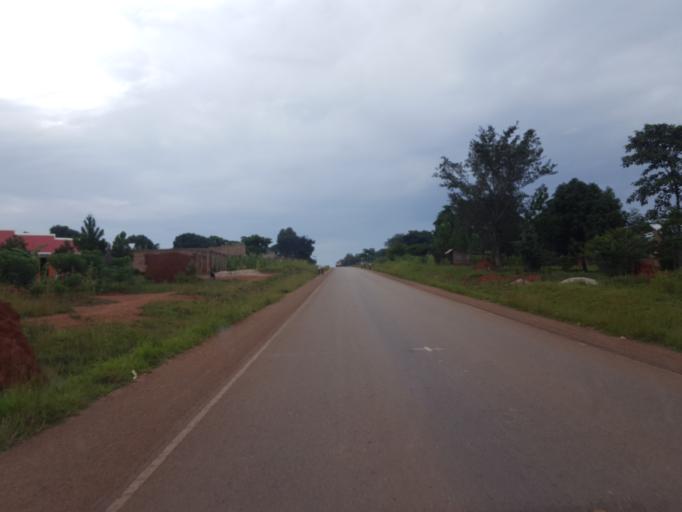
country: UG
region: Central Region
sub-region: Kyankwanzi District
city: Kyankwanzi
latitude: 1.1166
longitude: 31.6050
